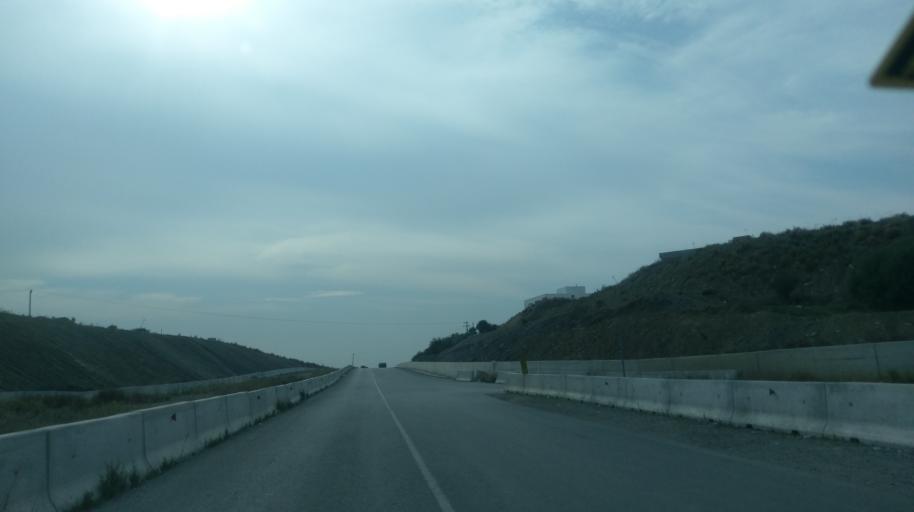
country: CY
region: Lefkosia
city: Nicosia
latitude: 35.2356
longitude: 33.3259
